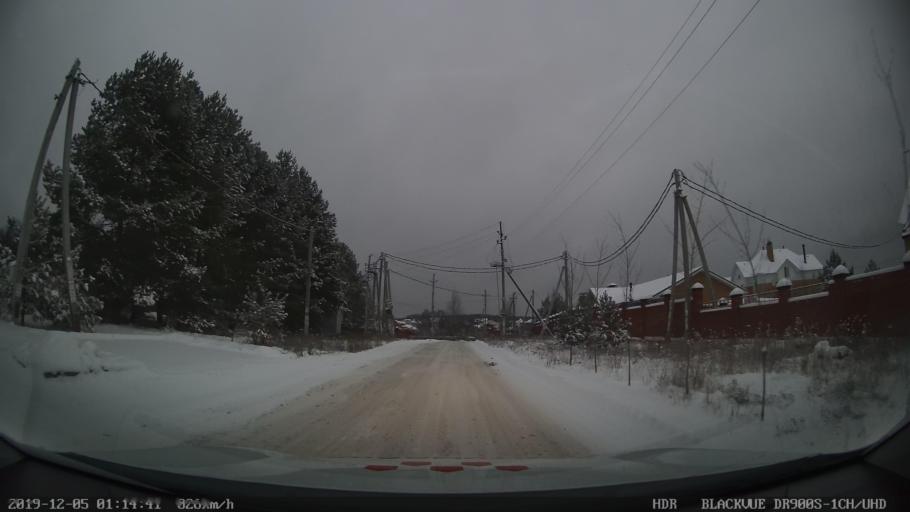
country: RU
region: Tatarstan
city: Stolbishchi
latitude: 55.6433
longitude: 49.1144
